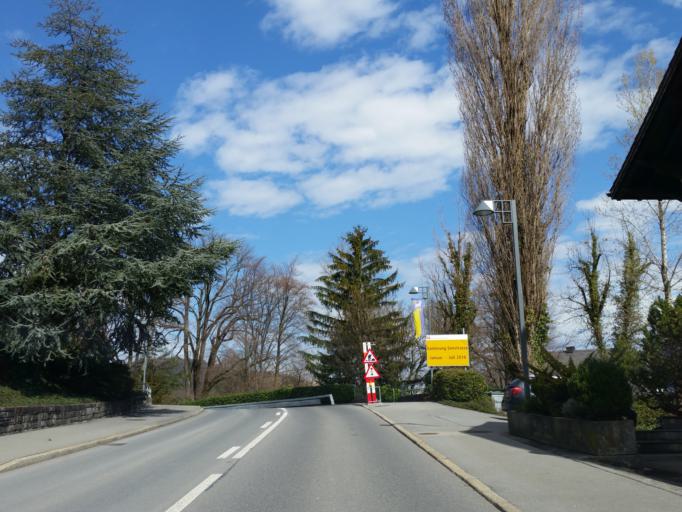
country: CH
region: Nidwalden
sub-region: Nidwalden
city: Hergiswil
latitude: 46.9898
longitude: 8.3151
